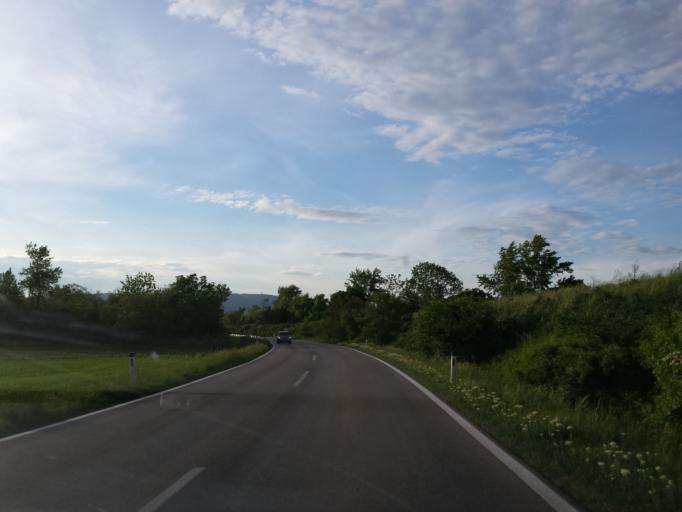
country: AT
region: Lower Austria
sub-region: Politischer Bezirk Baden
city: Oberwaltersdorf
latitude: 47.9874
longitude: 16.3042
